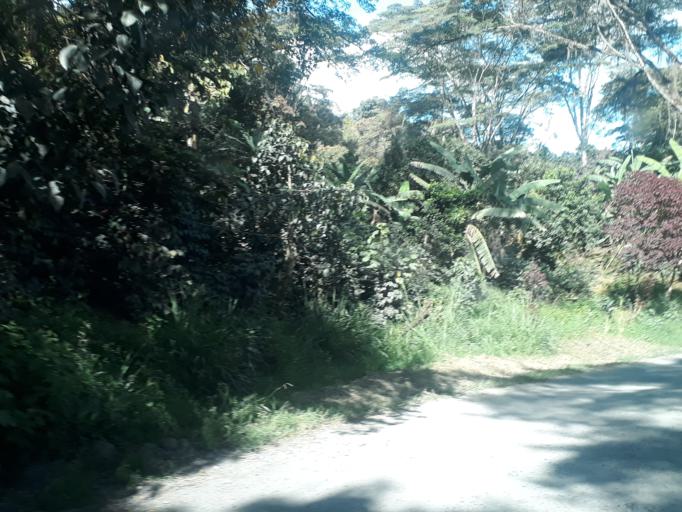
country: CO
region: Santander
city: Velez
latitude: 6.0534
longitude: -73.6497
